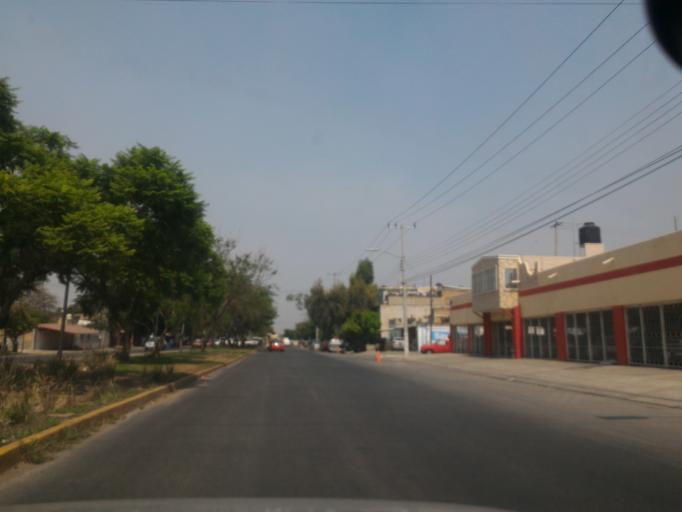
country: MX
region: Jalisco
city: Guadalajara
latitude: 20.6240
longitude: -103.3750
